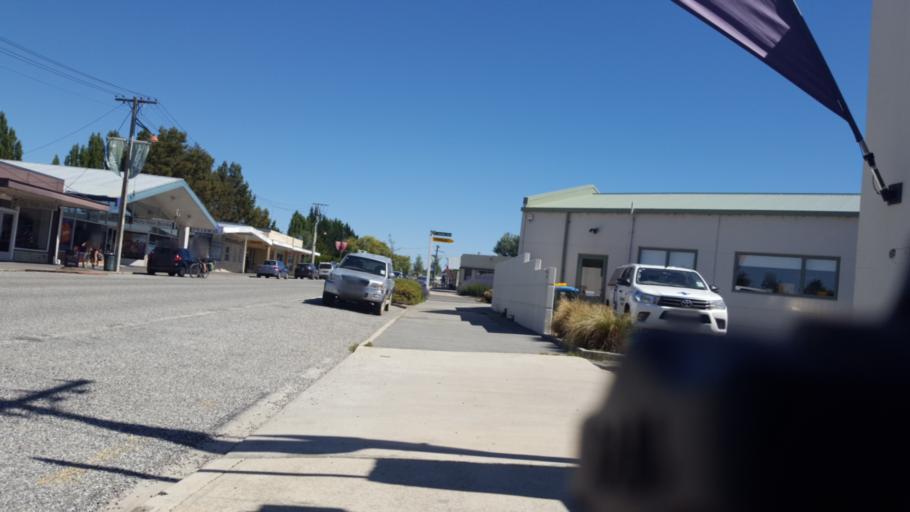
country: NZ
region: Otago
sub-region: Dunedin City
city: Dunedin
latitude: -45.1296
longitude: 170.0991
